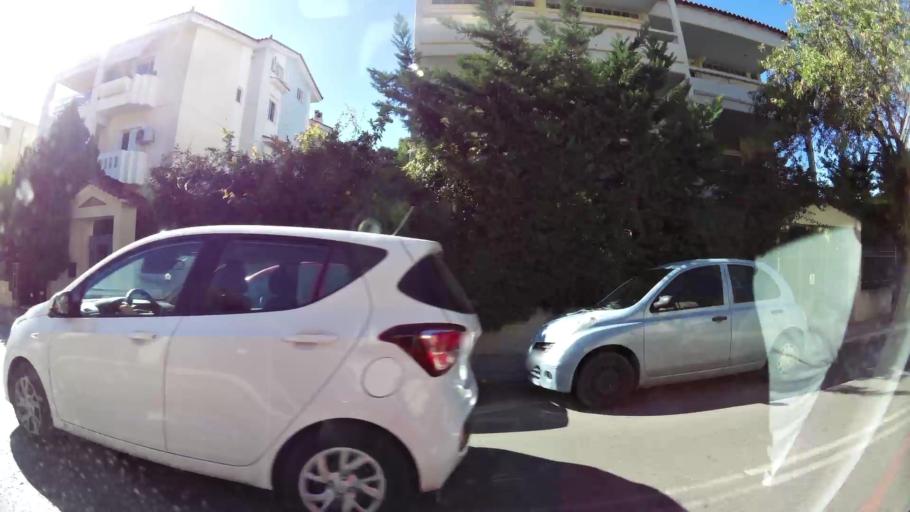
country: GR
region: Attica
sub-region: Nomarchia Anatolikis Attikis
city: Leondarion
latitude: 37.9837
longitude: 23.8561
